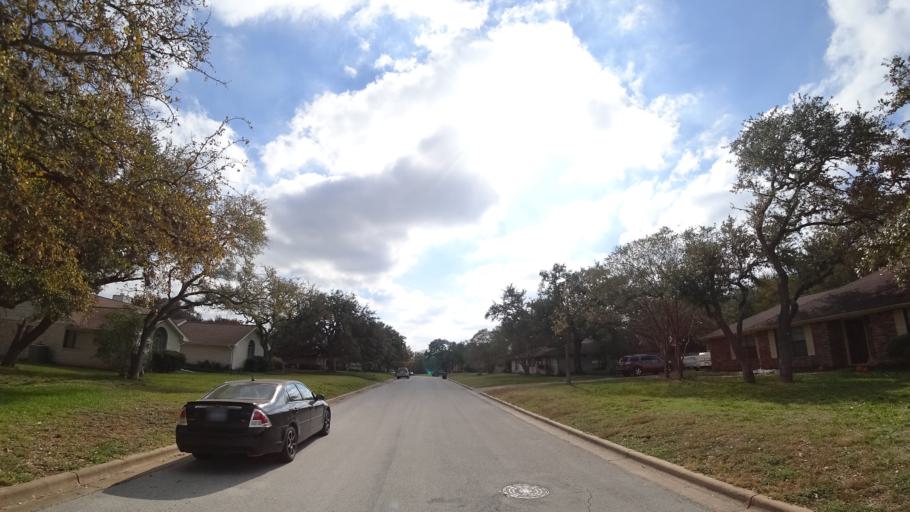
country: US
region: Texas
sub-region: Travis County
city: Shady Hollow
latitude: 30.1719
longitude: -97.8535
